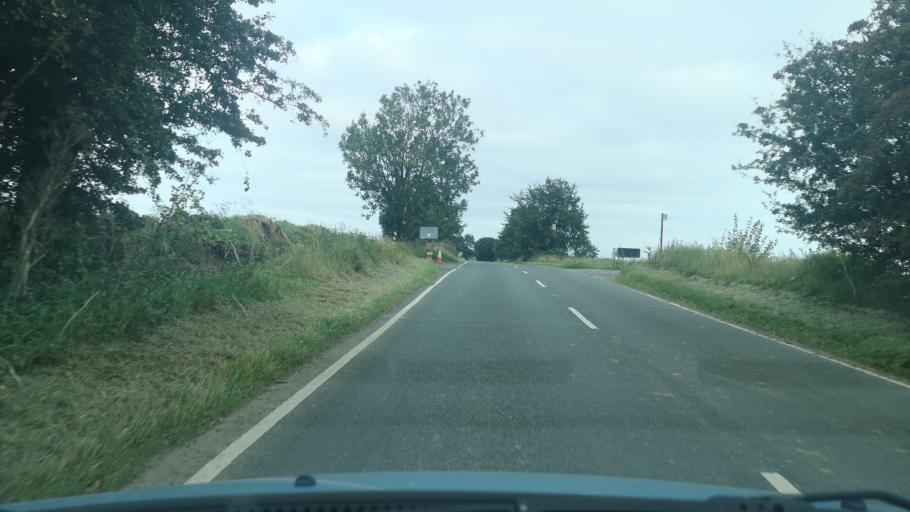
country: GB
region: England
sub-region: City and Borough of Wakefield
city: Darrington
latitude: 53.6569
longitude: -1.2662
